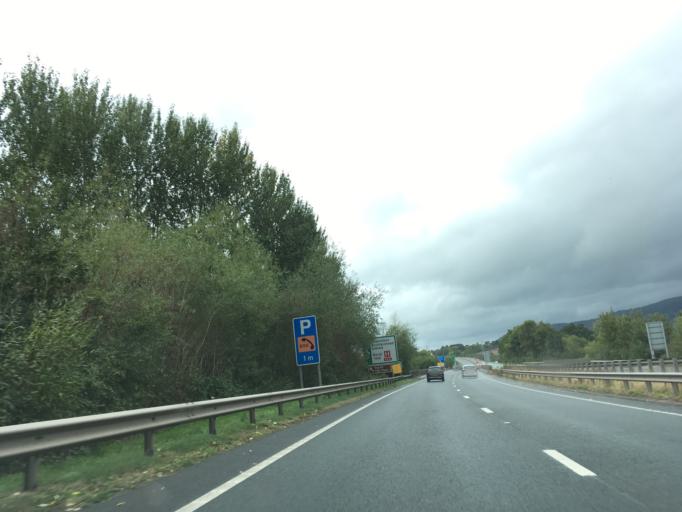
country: GB
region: Wales
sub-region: Monmouthshire
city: Abergavenny
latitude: 51.8109
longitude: -3.0149
